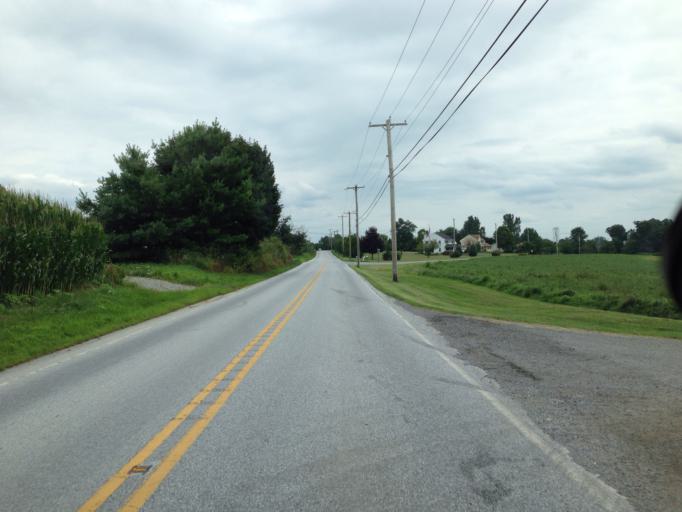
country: US
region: Pennsylvania
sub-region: Chester County
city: Oxford
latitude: 39.8338
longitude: -75.9298
